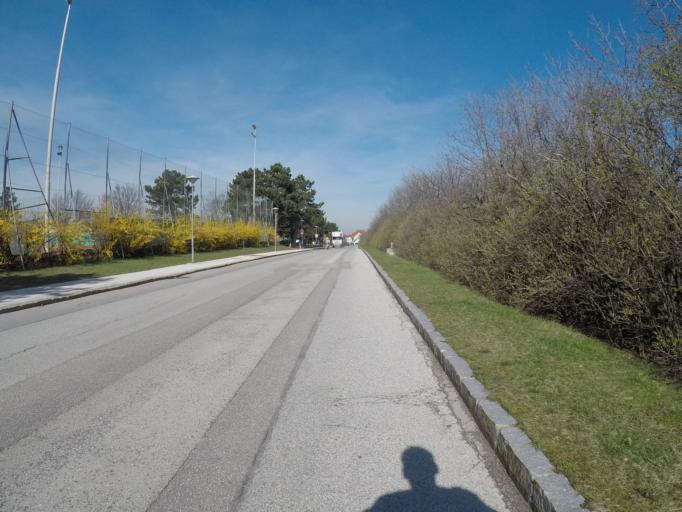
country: AT
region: Lower Austria
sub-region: Politischer Bezirk Modling
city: Vosendorf
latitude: 48.1166
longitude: 16.3373
